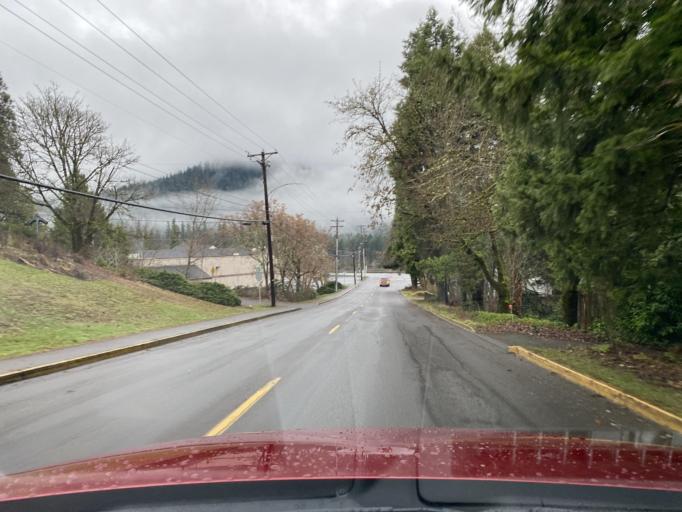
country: US
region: Oregon
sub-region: Lane County
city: Oakridge
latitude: 43.7461
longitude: -122.4671
